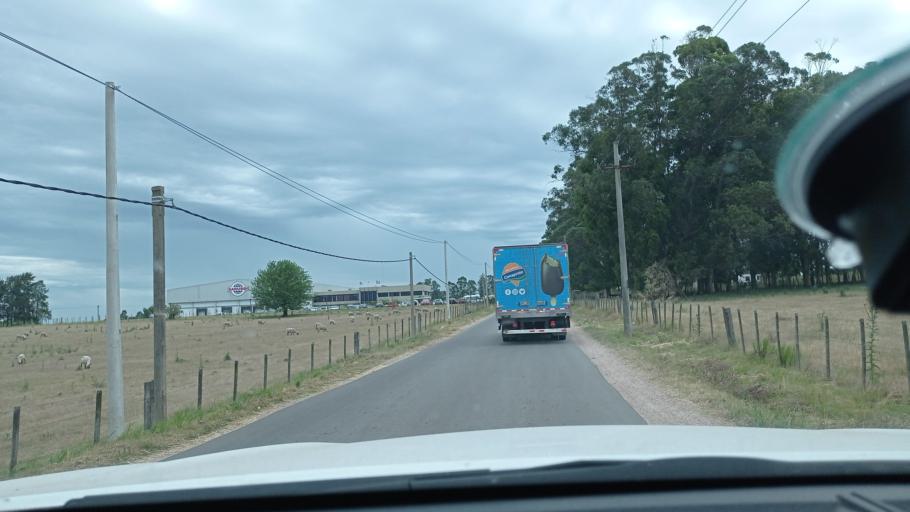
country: UY
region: Canelones
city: La Paz
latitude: -34.8040
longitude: -56.1867
